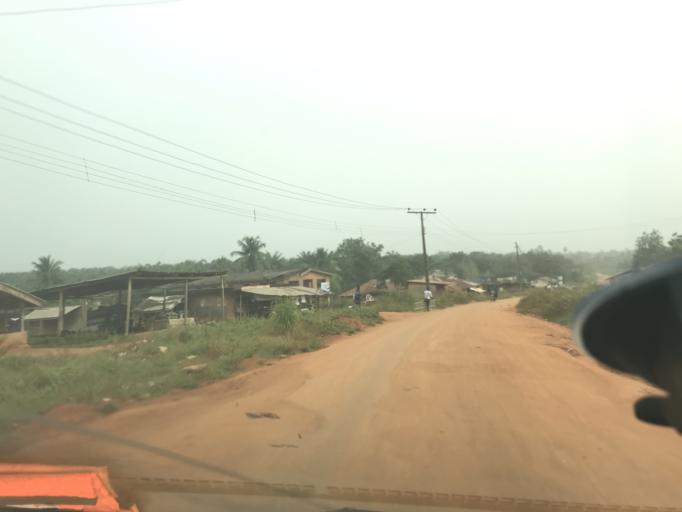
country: NG
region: Ogun
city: Ado Odo
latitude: 6.5816
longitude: 2.9310
